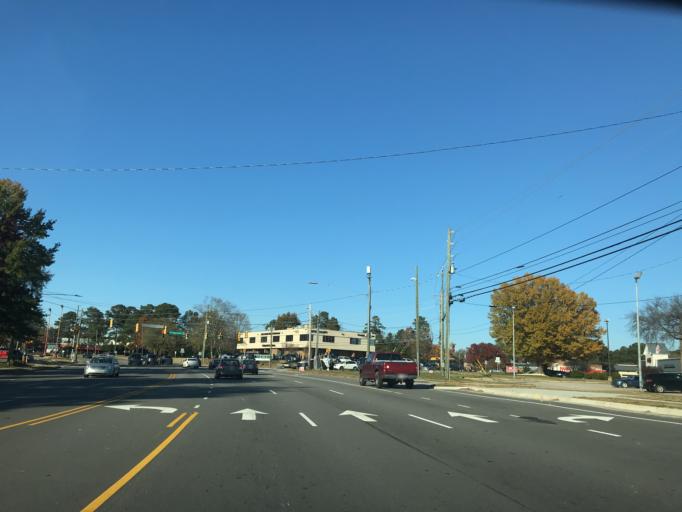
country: US
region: North Carolina
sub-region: Wake County
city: Raleigh
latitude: 35.8402
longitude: -78.6117
